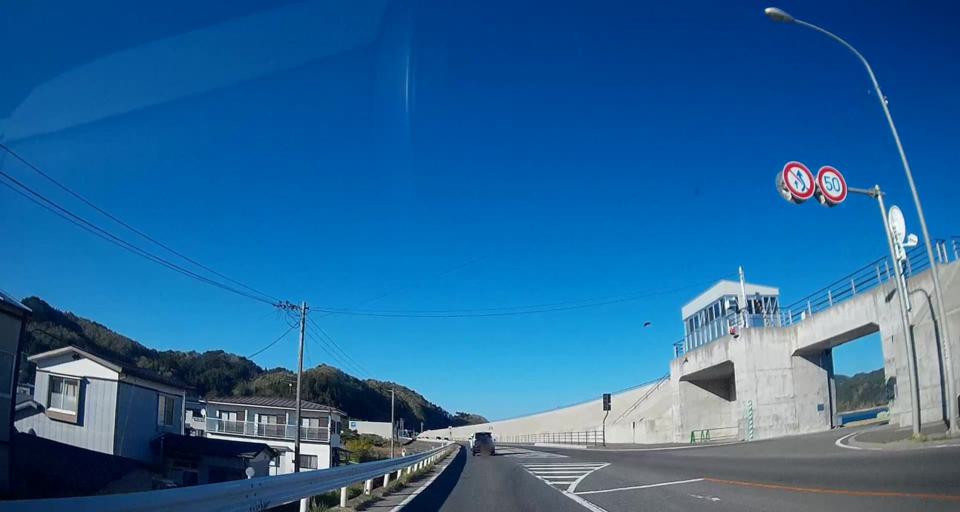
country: JP
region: Iwate
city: Miyako
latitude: 39.6050
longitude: 141.9547
